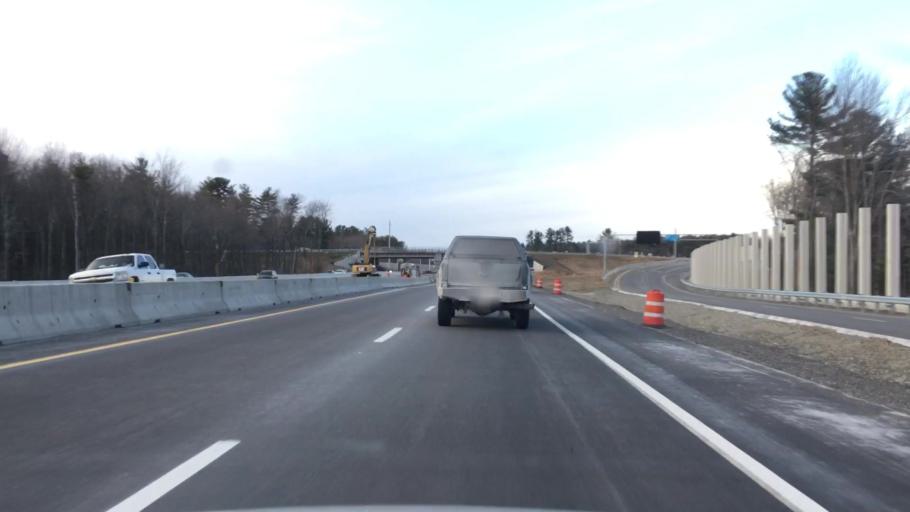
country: US
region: Maine
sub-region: York County
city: Eliot
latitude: 43.1280
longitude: -70.8375
